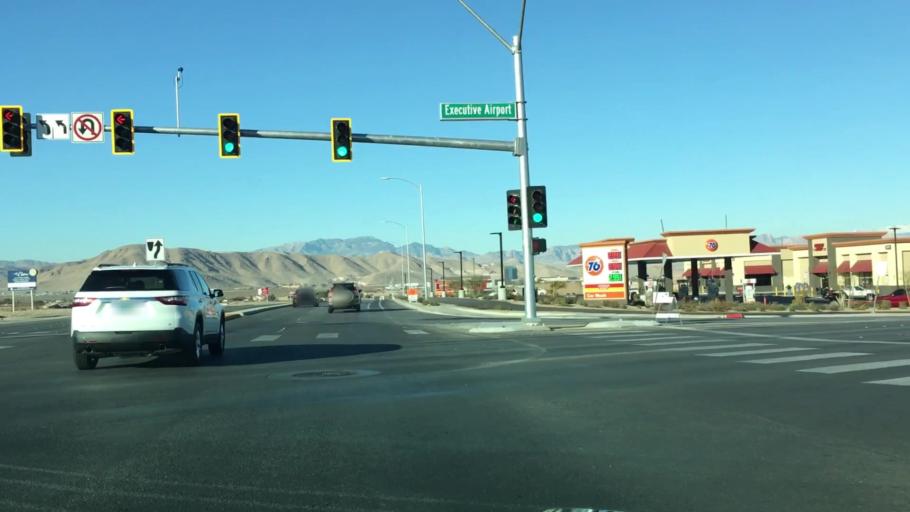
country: US
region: Nevada
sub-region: Clark County
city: Enterprise
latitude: 35.9599
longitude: -115.1394
